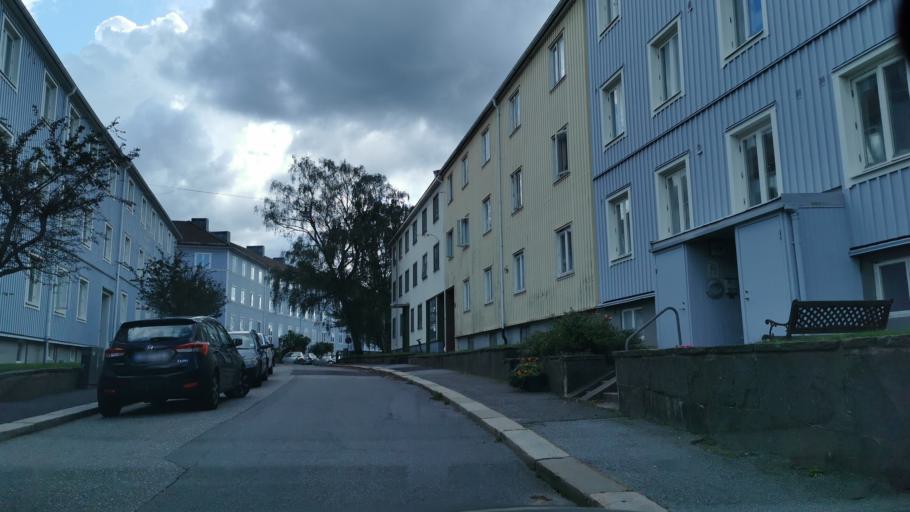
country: SE
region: Vaestra Goetaland
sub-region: Goteborg
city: Goeteborg
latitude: 57.6888
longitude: 11.9715
